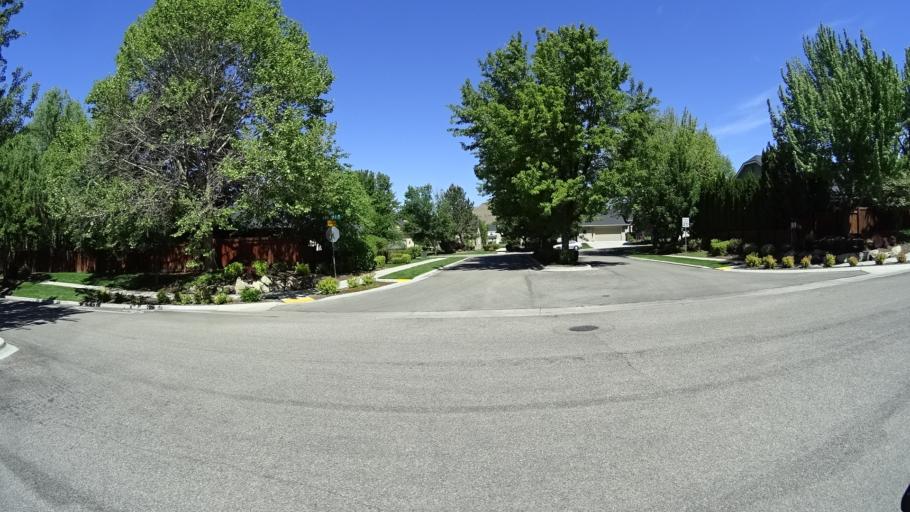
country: US
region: Idaho
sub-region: Ada County
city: Boise
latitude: 43.5698
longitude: -116.1199
